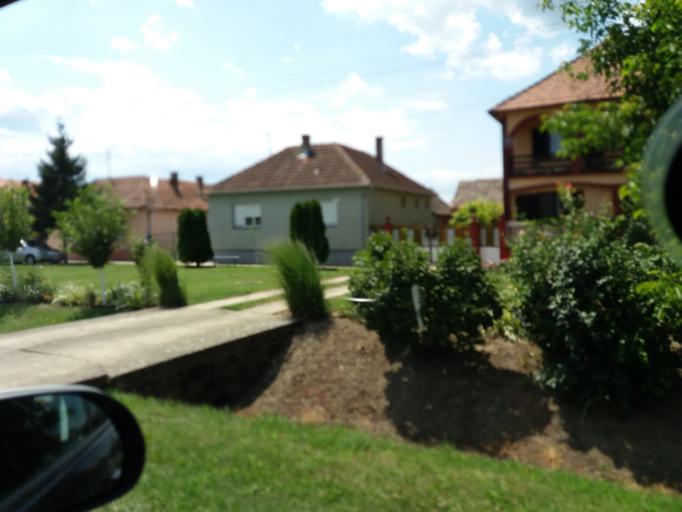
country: RS
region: Autonomna Pokrajina Vojvodina
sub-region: Sremski Okrug
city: Pecinci
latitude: 44.8513
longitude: 19.9614
